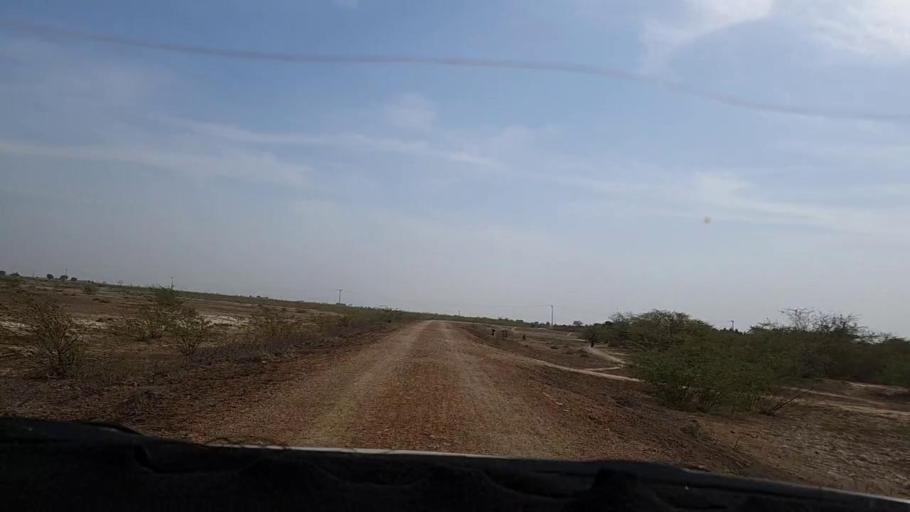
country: PK
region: Sindh
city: Pithoro
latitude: 25.5266
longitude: 69.3475
